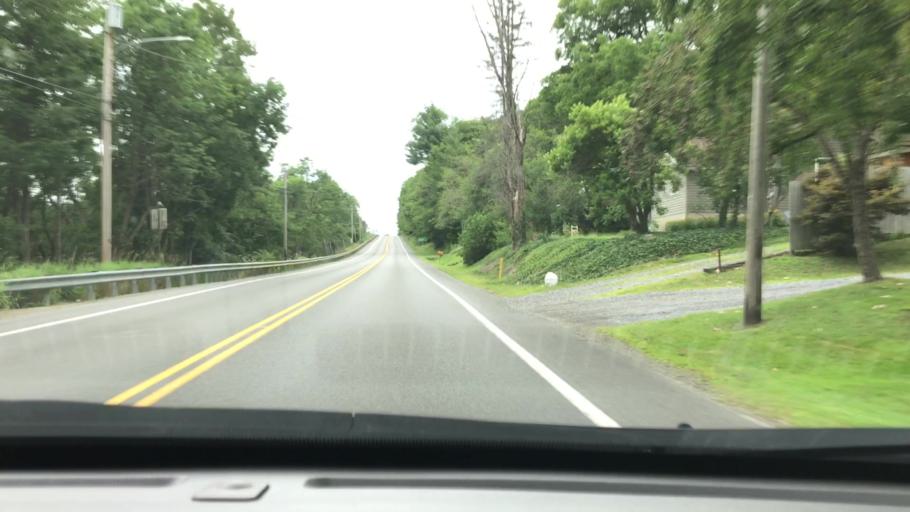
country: US
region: Pennsylvania
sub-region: Elk County
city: Johnsonburg
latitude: 41.5811
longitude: -78.6883
